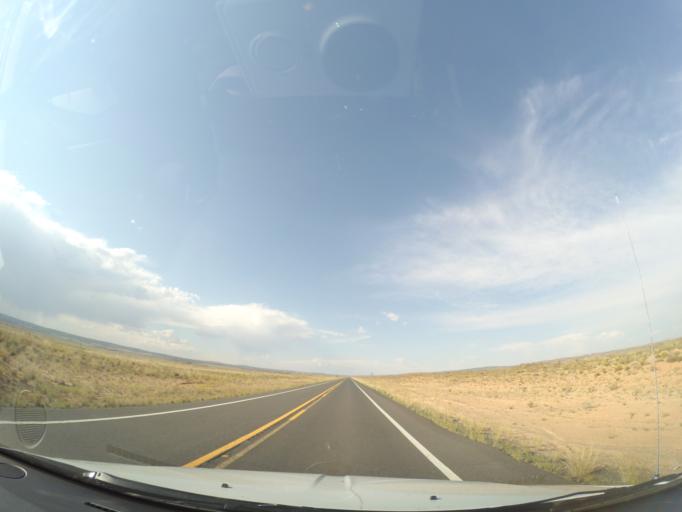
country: US
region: Arizona
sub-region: Coconino County
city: Tuba City
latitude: 36.4100
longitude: -111.4237
